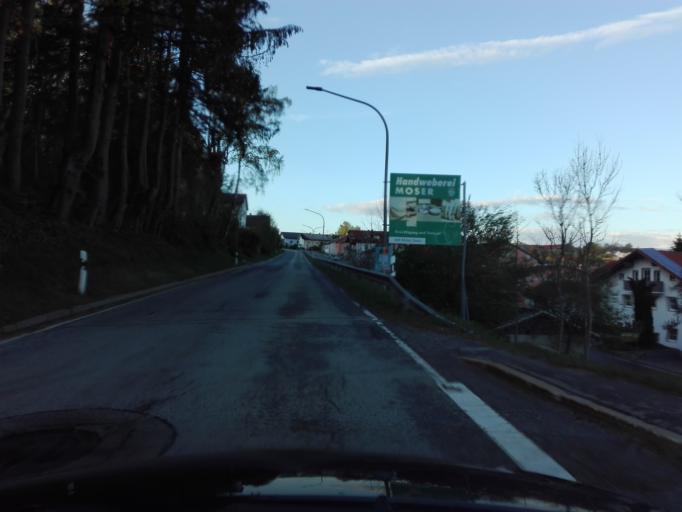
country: DE
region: Bavaria
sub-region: Lower Bavaria
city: Wegscheid
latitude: 48.5960
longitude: 13.7835
